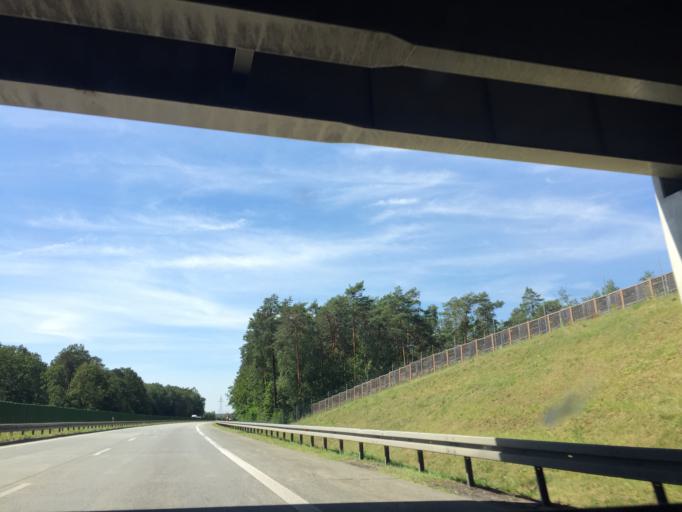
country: PL
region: Lodz Voivodeship
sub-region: Powiat piotrkowski
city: Moszczenica
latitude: 51.4493
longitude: 19.7638
